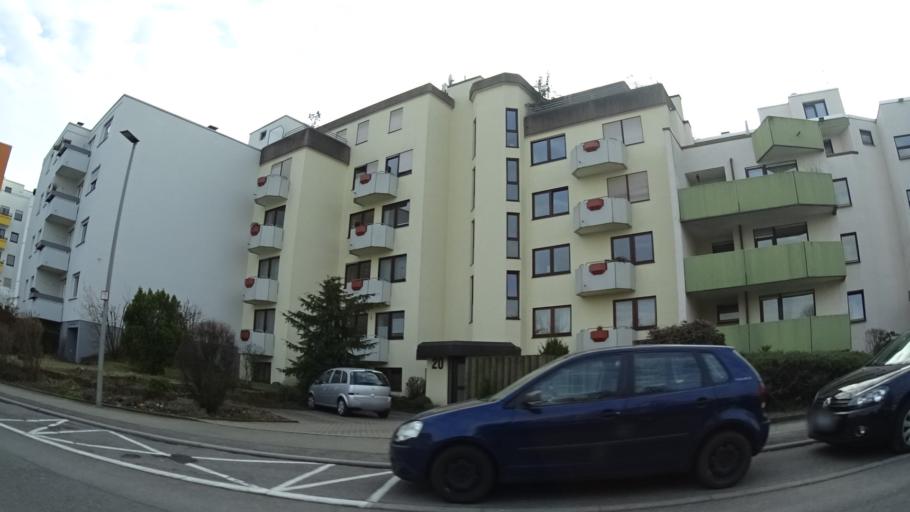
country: DE
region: Baden-Wuerttemberg
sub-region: Regierungsbezirk Stuttgart
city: Steinenbronn
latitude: 48.7190
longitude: 9.0913
